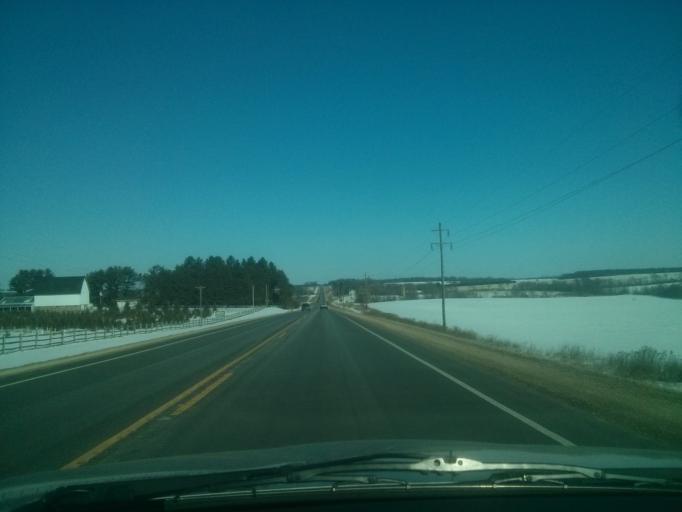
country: US
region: Wisconsin
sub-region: Polk County
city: Clear Lake
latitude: 45.1406
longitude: -92.2817
